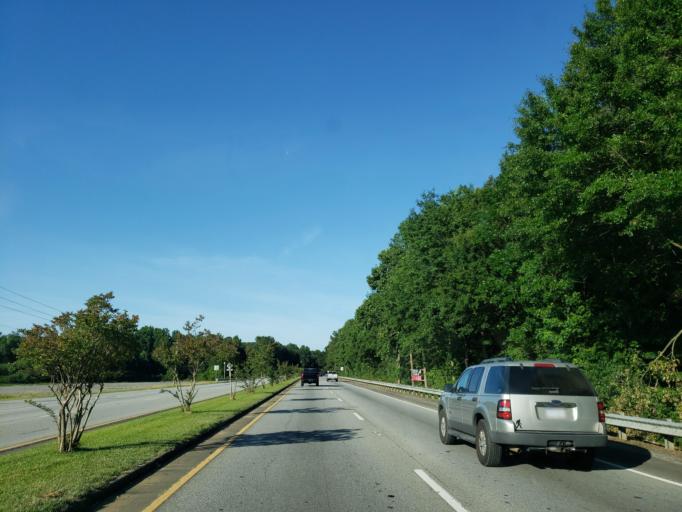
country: US
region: Georgia
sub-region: Floyd County
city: Rome
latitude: 34.2848
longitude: -85.1641
